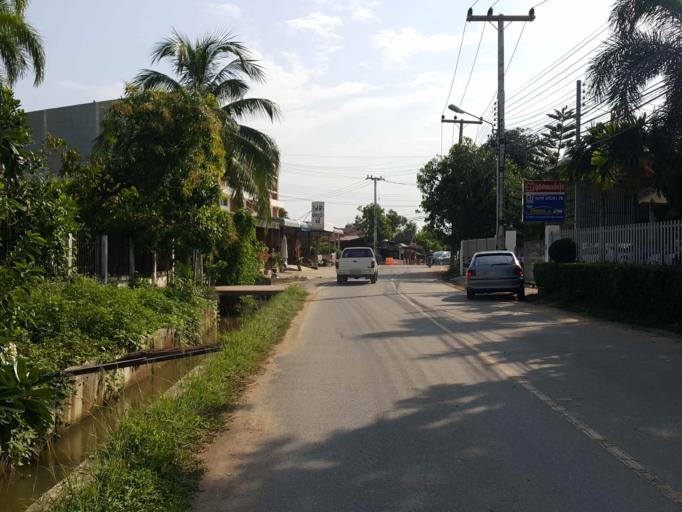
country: TH
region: Chiang Mai
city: San Sai
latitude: 18.8303
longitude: 99.0332
